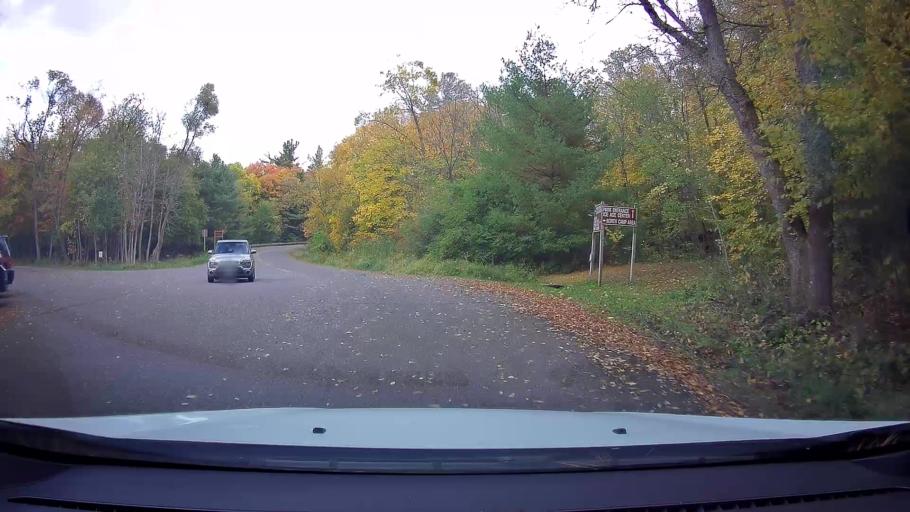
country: US
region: Wisconsin
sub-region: Polk County
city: Saint Croix Falls
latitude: 45.3996
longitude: -92.6474
